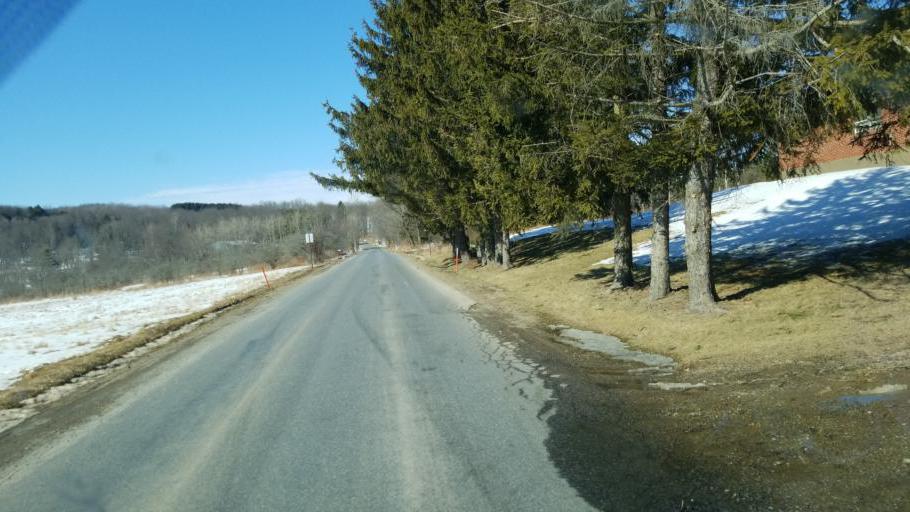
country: US
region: Pennsylvania
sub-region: Tioga County
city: Westfield
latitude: 41.9821
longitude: -77.6684
